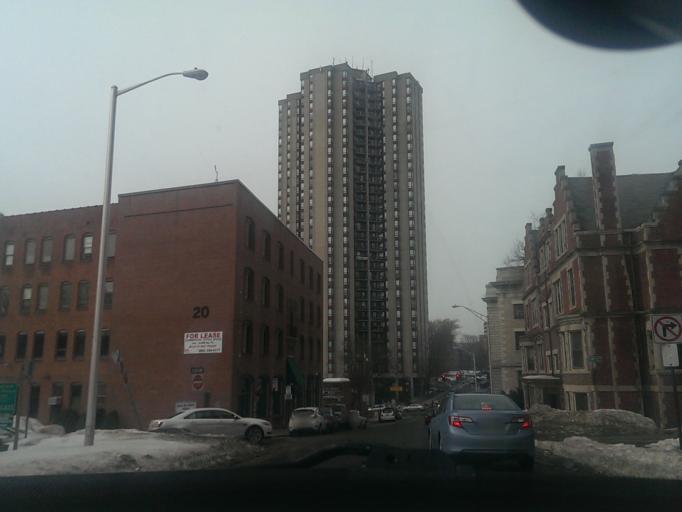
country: US
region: Massachusetts
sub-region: Hampden County
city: Springfield
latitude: 42.1022
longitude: -72.5836
